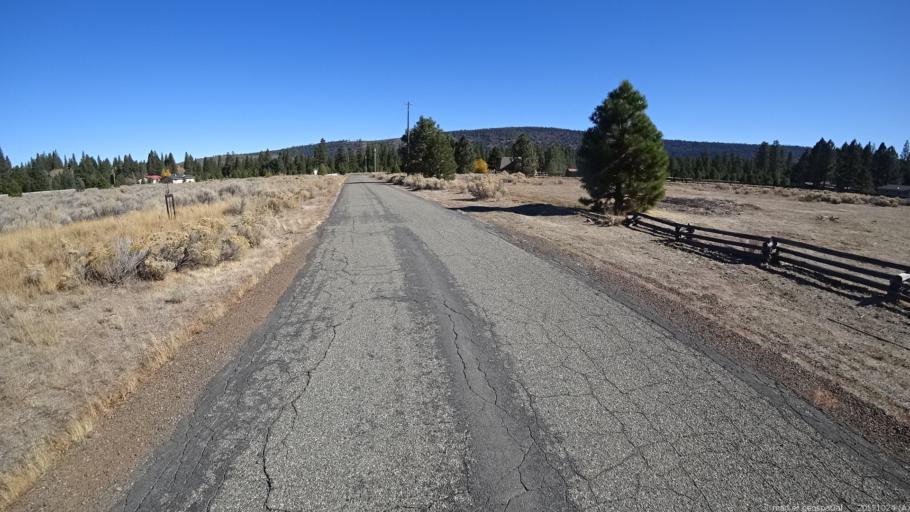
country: US
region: California
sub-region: Shasta County
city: Burney
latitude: 40.6737
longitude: -121.4299
